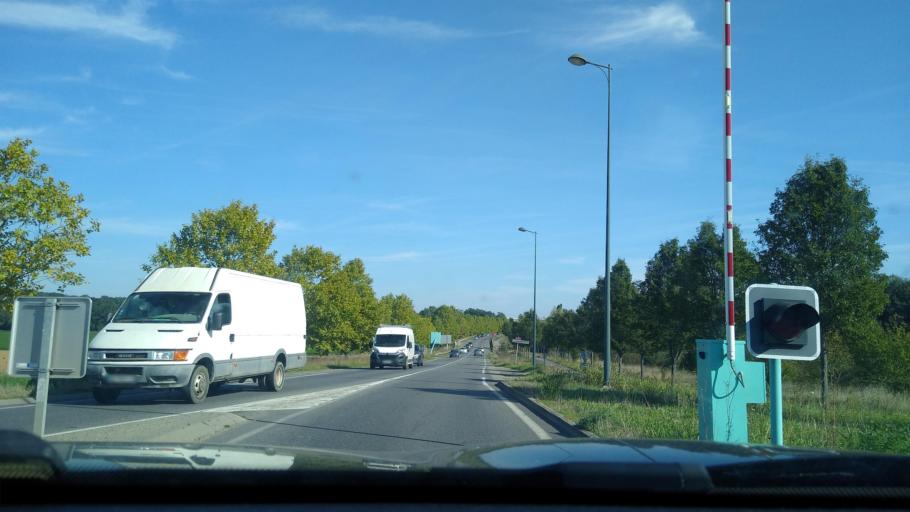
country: FR
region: Midi-Pyrenees
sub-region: Departement de la Haute-Garonne
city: Cornebarrieu
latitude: 43.6613
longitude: 1.3254
